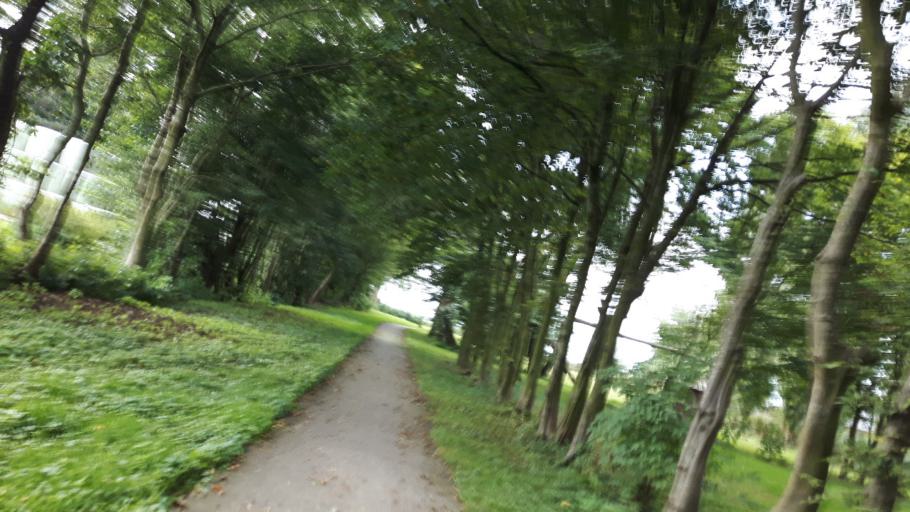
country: NL
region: Friesland
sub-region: Gemeente Leeuwarden
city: Camminghaburen
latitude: 53.2429
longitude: 5.8338
